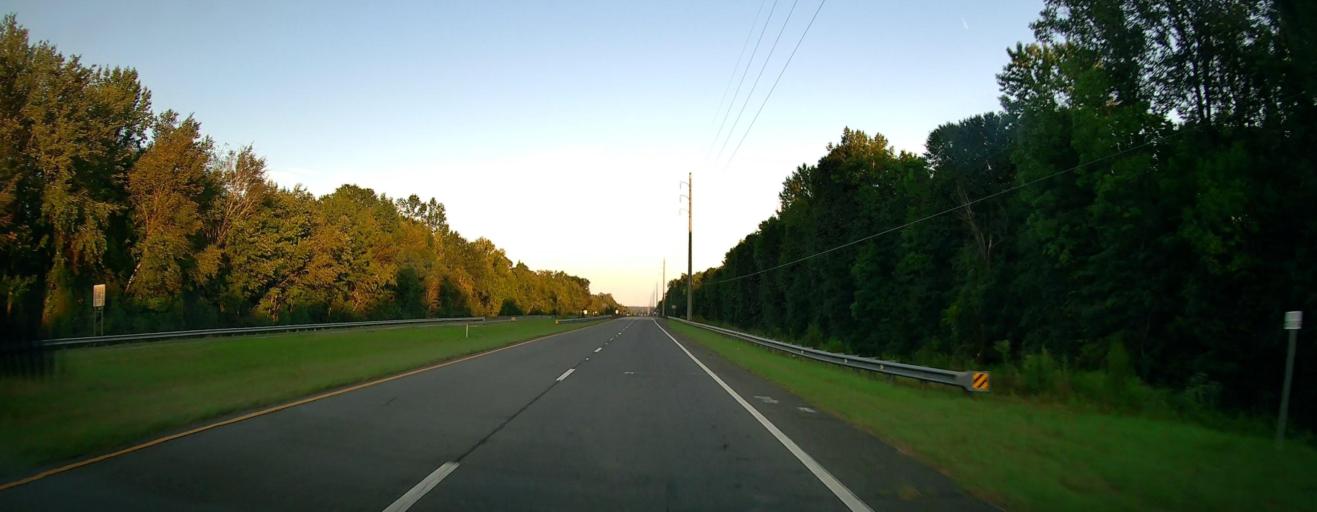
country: US
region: Georgia
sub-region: Taylor County
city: Reynolds
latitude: 32.5512
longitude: -84.0497
